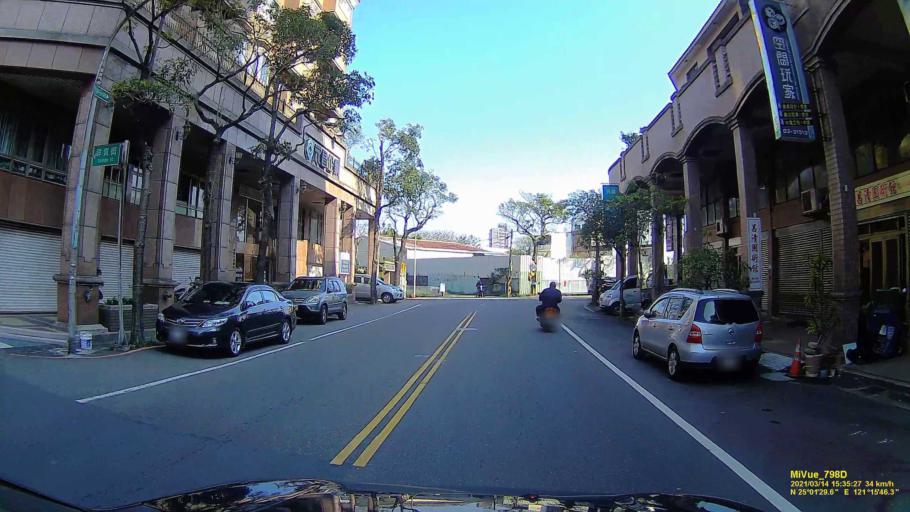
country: TW
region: Taiwan
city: Taoyuan City
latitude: 25.0248
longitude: 121.2629
